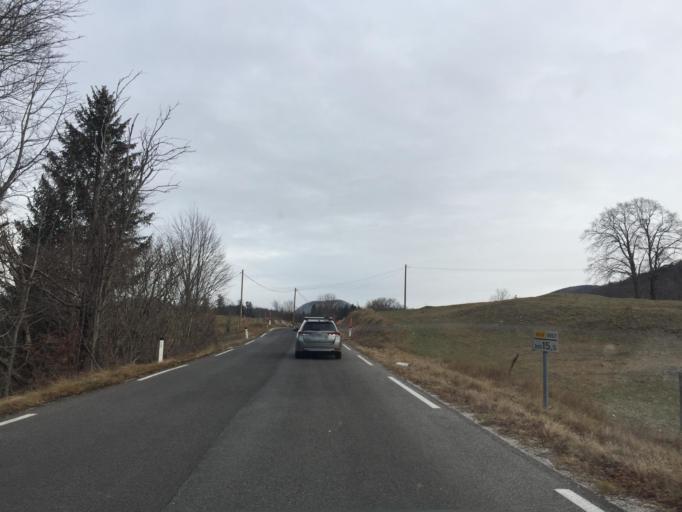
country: SI
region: Nova Gorica
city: Sempas
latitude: 45.9892
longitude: 13.7690
